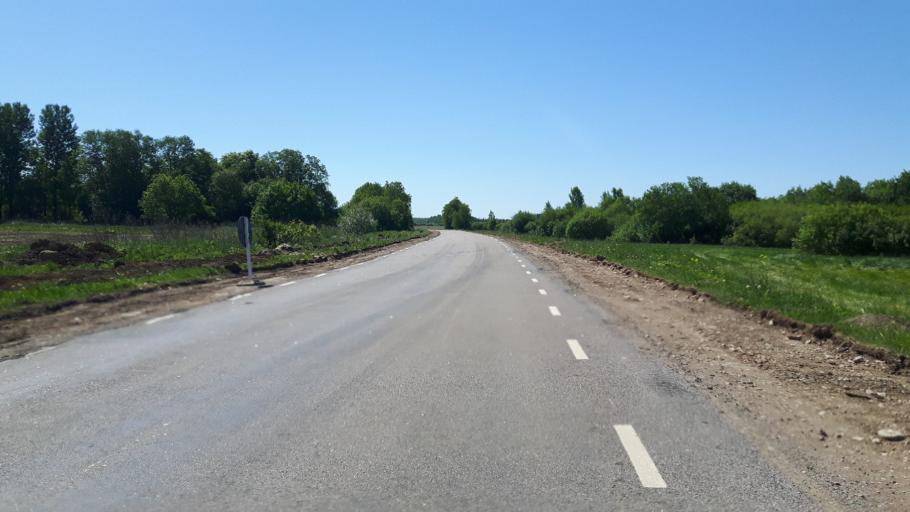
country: EE
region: Ida-Virumaa
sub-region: Narva-Joesuu linn
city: Narva-Joesuu
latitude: 59.3909
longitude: 27.9219
